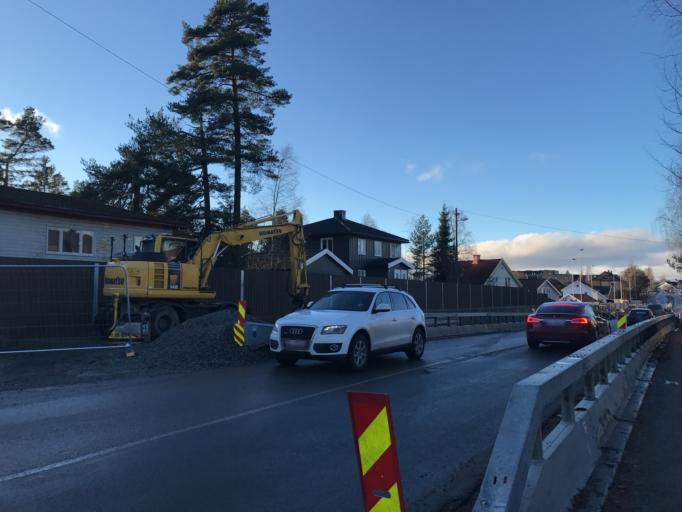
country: NO
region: Akershus
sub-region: Ullensaker
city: Jessheim
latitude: 60.1407
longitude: 11.1833
